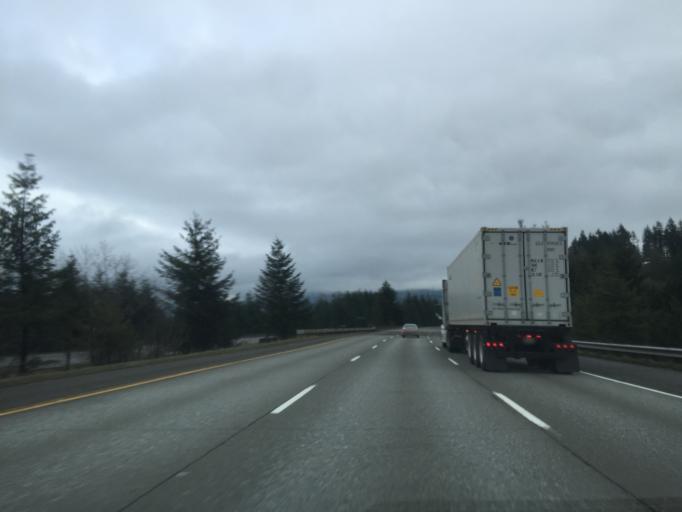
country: US
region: Washington
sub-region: King County
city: North Bend
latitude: 47.4893
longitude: -121.7980
